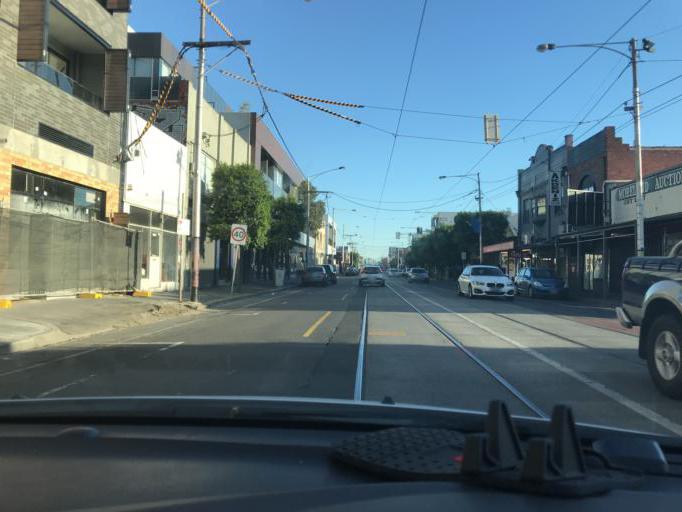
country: AU
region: Victoria
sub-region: Moreland
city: Coburg
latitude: -37.7577
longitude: 144.9638
